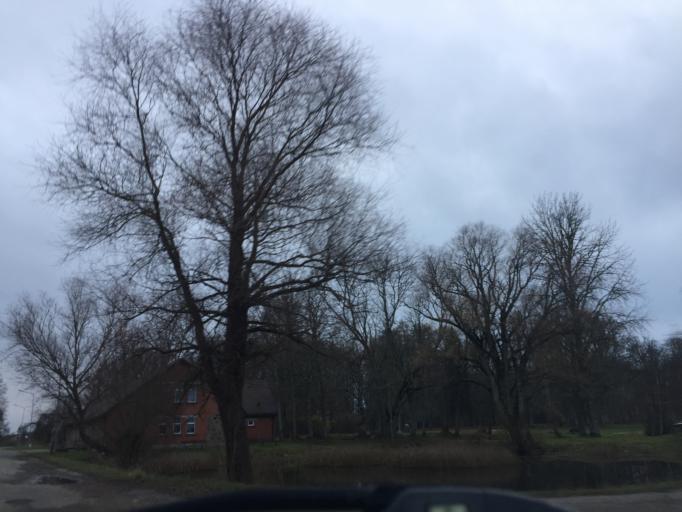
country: LV
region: Aloja
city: Aloja
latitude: 57.6909
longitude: 24.8838
